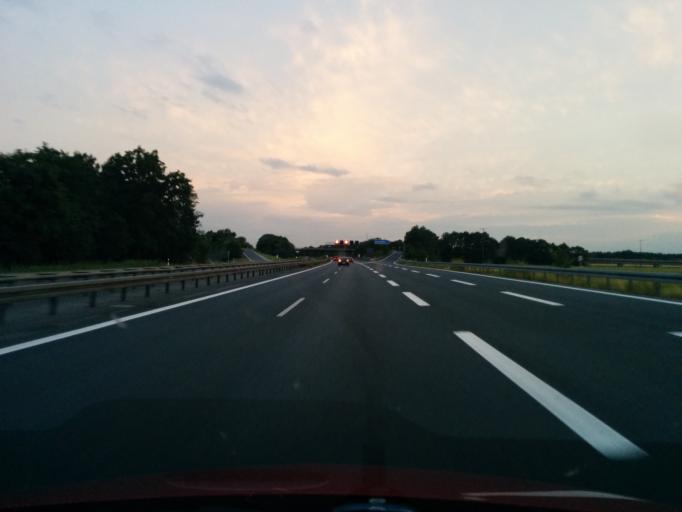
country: DE
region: Bavaria
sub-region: Regierungsbezirk Mittelfranken
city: Bubenreuth
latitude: 49.6399
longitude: 11.0140
